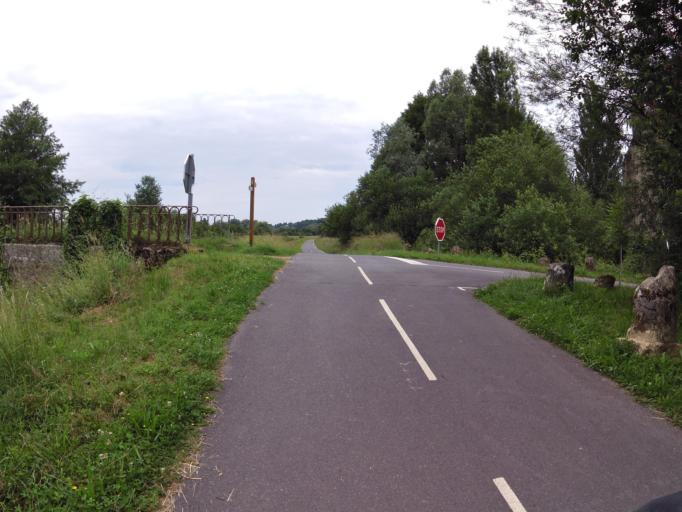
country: FR
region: Champagne-Ardenne
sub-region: Departement des Ardennes
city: Saint-Laurent
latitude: 49.7501
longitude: 4.7675
